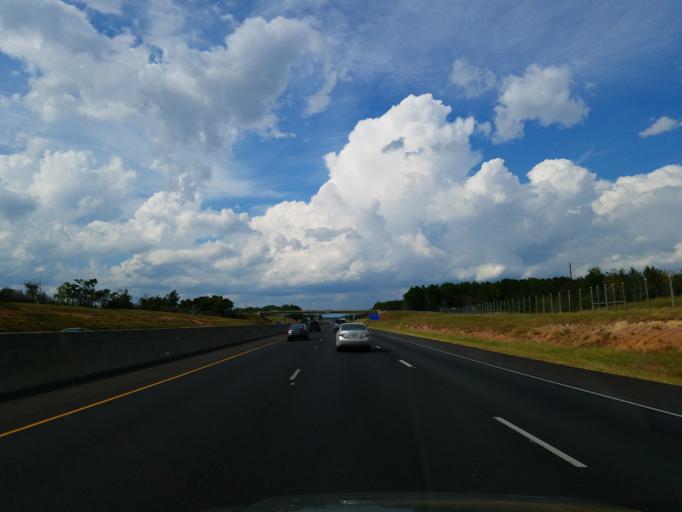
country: US
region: Georgia
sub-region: Tift County
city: Tifton
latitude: 31.5289
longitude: -83.5229
